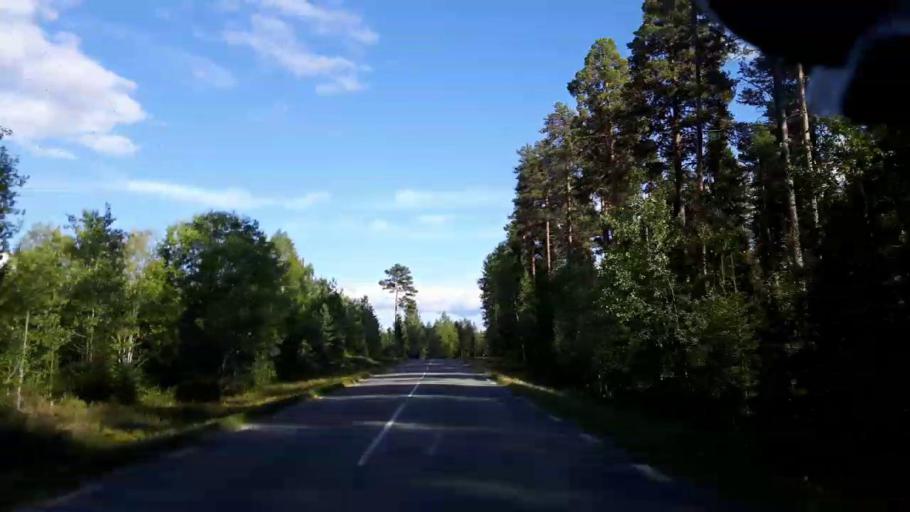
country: SE
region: Jaemtland
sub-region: Stroemsunds Kommun
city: Stroemsund
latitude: 63.3751
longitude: 15.5625
